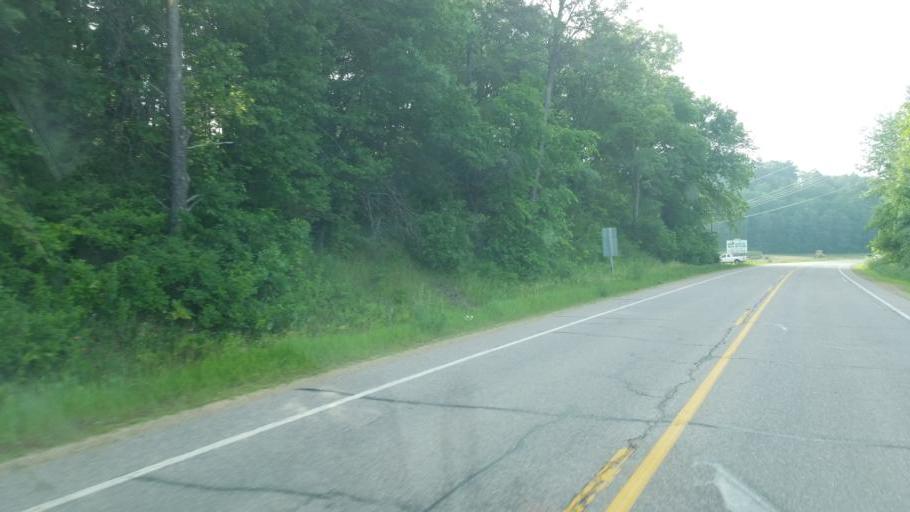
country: US
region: Wisconsin
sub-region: Juneau County
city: Elroy
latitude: 43.6783
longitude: -90.2562
